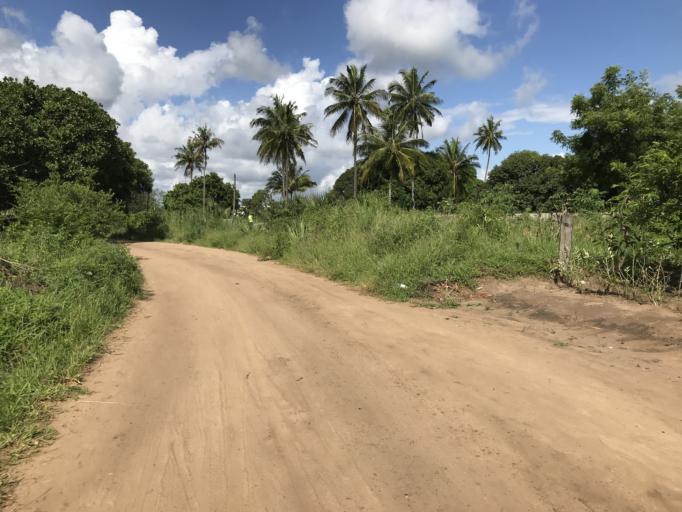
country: TZ
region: Dar es Salaam
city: Dar es Salaam
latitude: -6.8903
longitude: 39.4300
